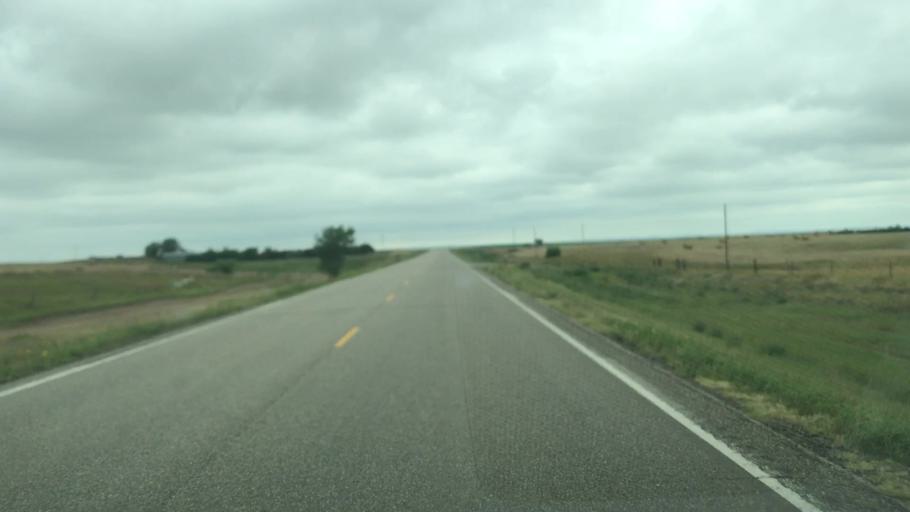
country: US
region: South Dakota
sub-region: Jackson County
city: Kadoka
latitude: 43.8237
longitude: -101.5224
